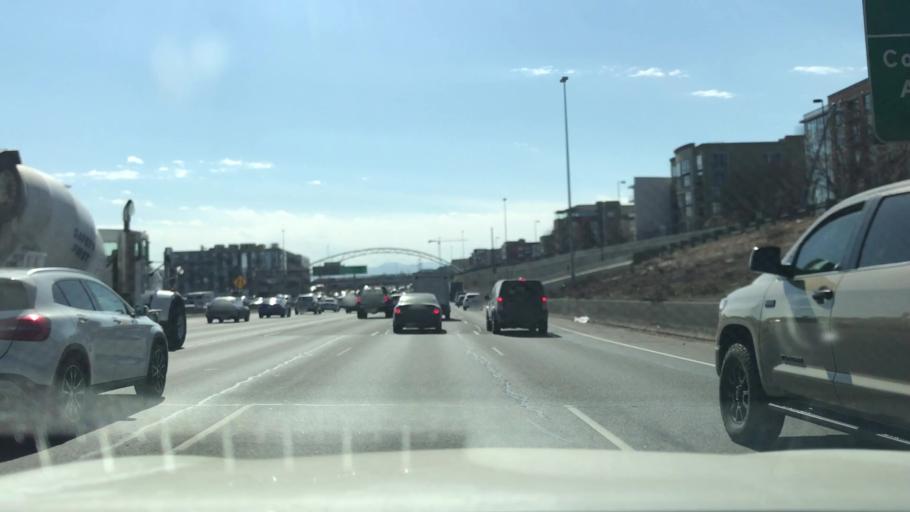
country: US
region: Colorado
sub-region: Denver County
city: Denver
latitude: 39.7606
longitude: -105.0064
